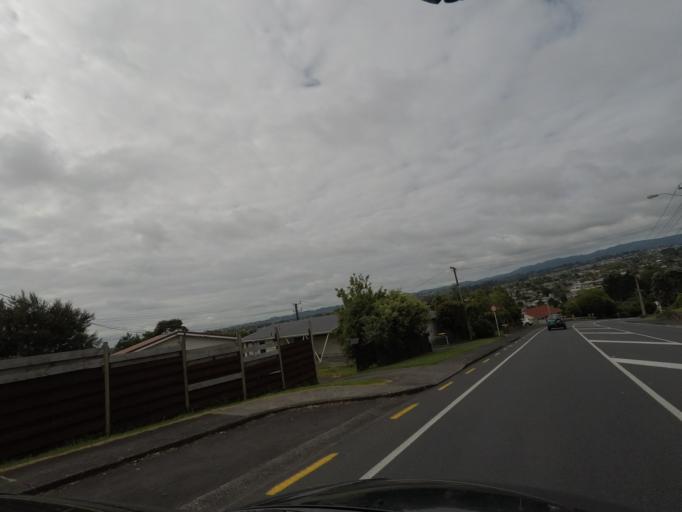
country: NZ
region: Auckland
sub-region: Auckland
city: Rosebank
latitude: -36.8550
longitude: 174.6120
